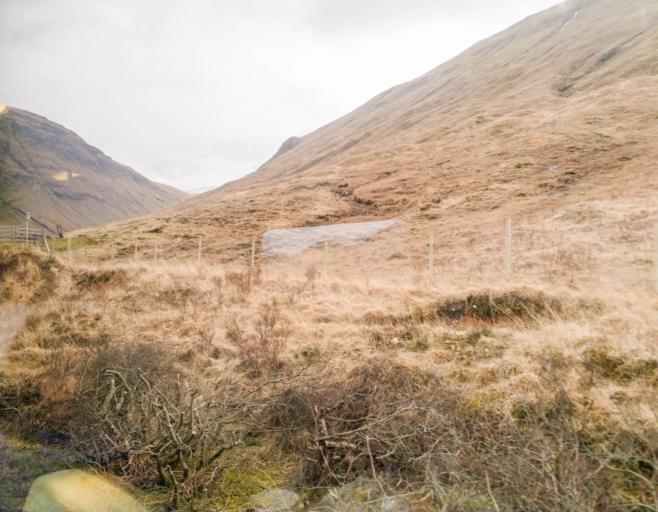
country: GB
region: Scotland
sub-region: Argyll and Bute
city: Garelochhead
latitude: 56.4802
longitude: -4.7117
